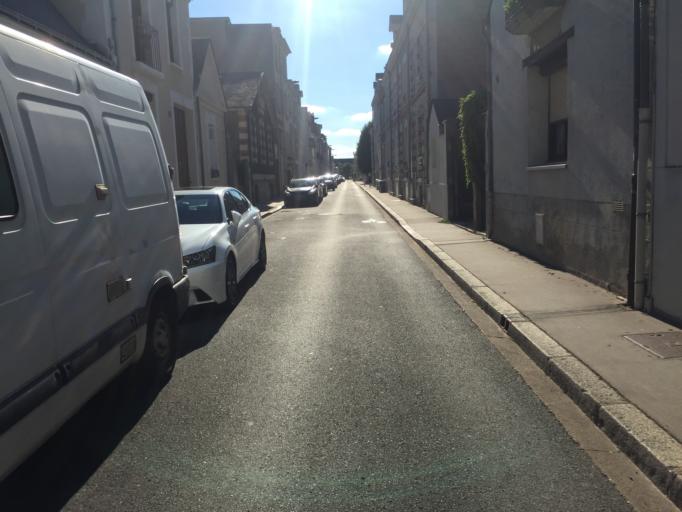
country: FR
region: Centre
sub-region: Departement d'Indre-et-Loire
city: Tours
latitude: 47.3850
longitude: 0.6822
